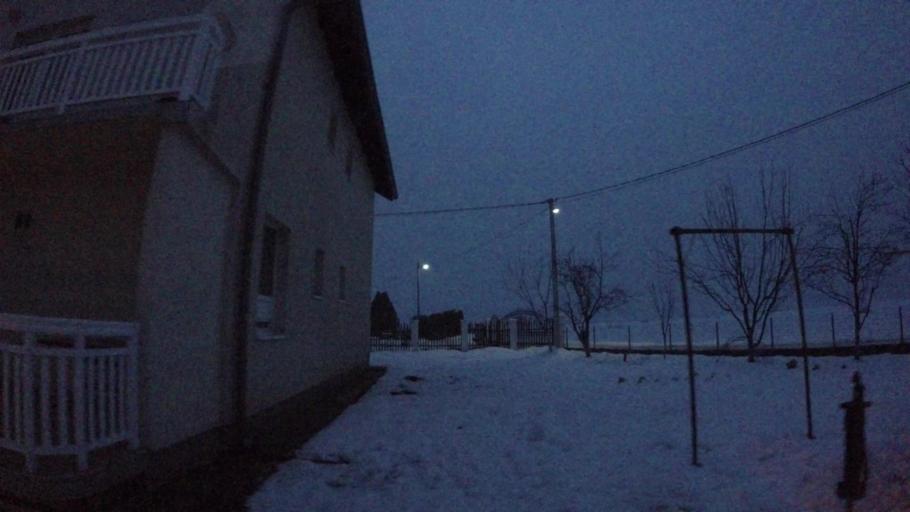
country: BA
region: Federation of Bosnia and Herzegovina
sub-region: Kanton Sarajevo
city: Sarajevo
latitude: 43.8589
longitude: 18.2931
